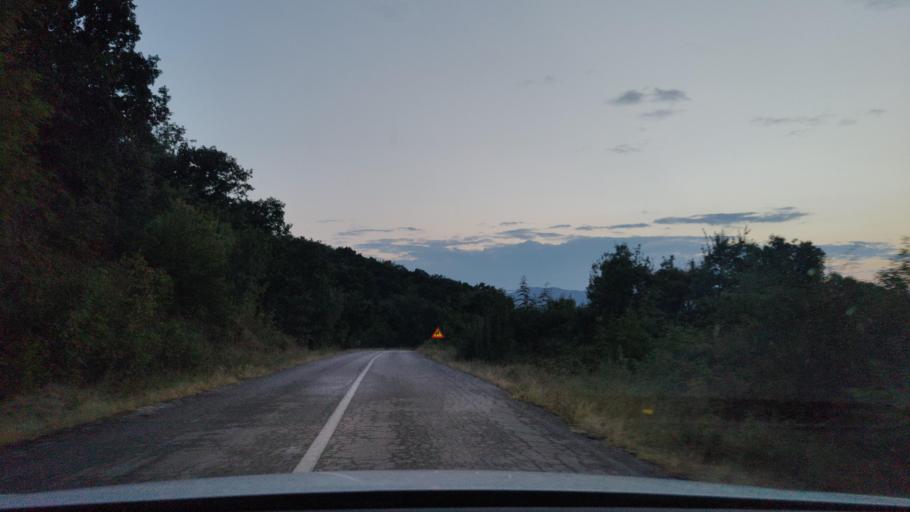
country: GR
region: Central Macedonia
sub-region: Nomos Serron
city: Chrysochorafa
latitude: 41.1806
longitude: 23.1490
